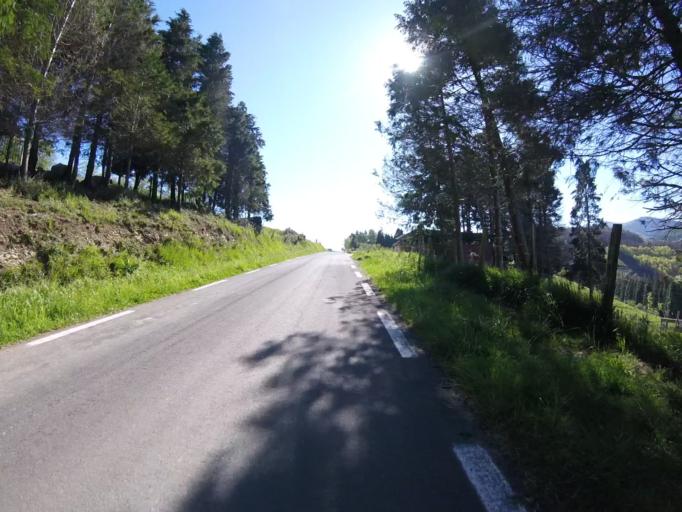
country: ES
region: Basque Country
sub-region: Provincia de Guipuzcoa
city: Aizarnazabal
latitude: 43.2141
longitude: -2.2062
